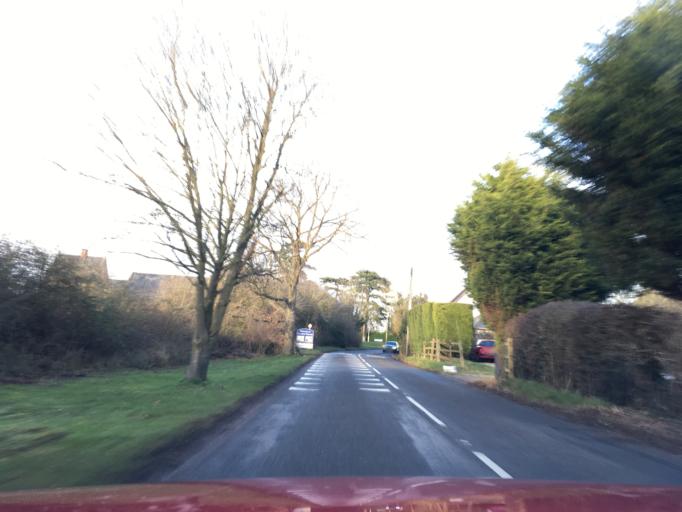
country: GB
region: England
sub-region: Warwickshire
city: Henley in Arden
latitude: 52.2637
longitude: -1.7850
